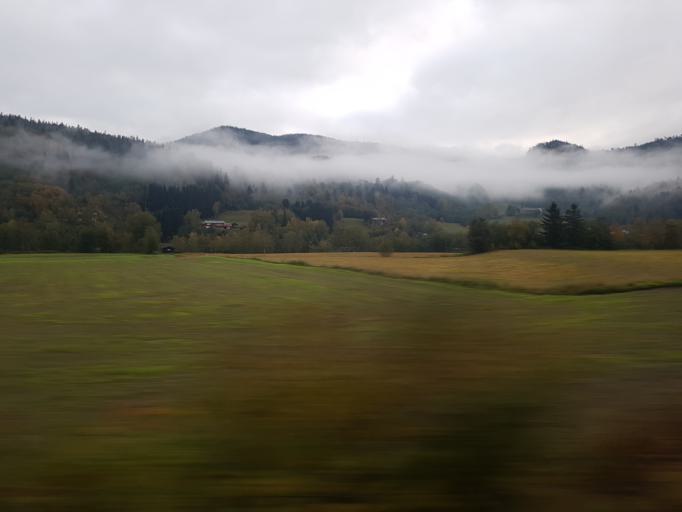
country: NO
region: Sor-Trondelag
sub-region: Midtre Gauldal
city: Storen
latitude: 63.0919
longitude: 10.2411
